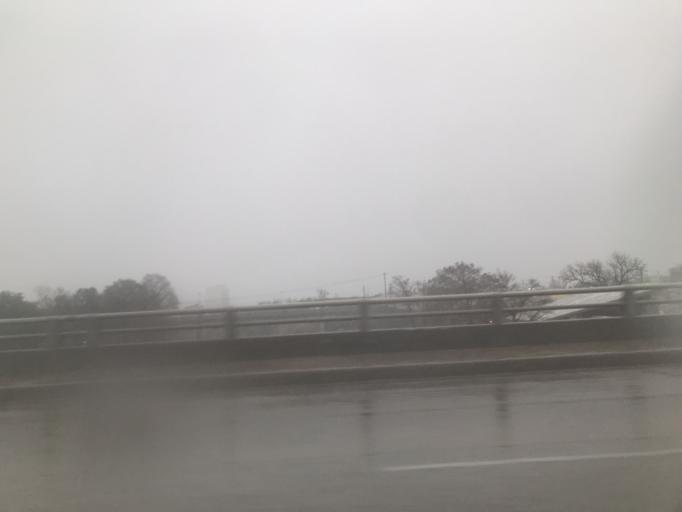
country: US
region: Texas
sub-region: Tom Green County
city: San Angelo
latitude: 31.4577
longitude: -100.4347
